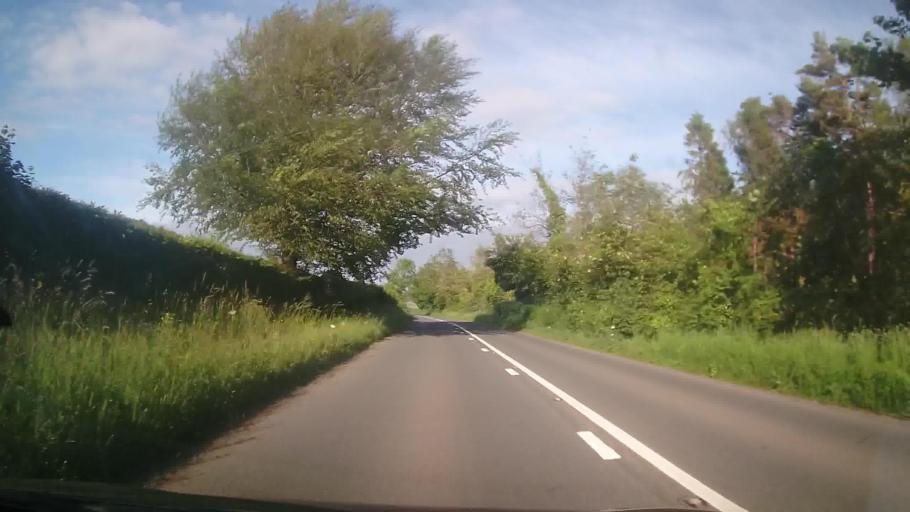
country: GB
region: England
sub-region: Devon
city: Ivybridge
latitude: 50.3505
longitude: -3.9489
